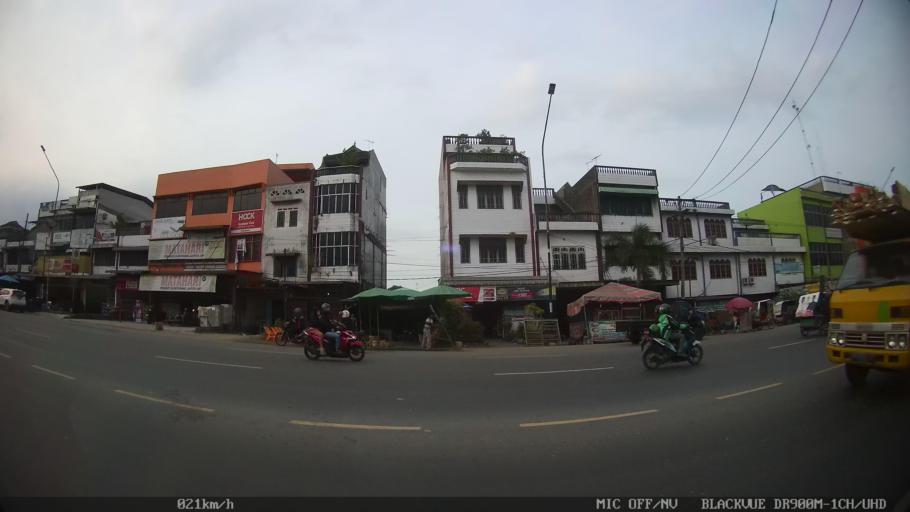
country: ID
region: North Sumatra
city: Sunggal
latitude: 3.5991
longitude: 98.6064
